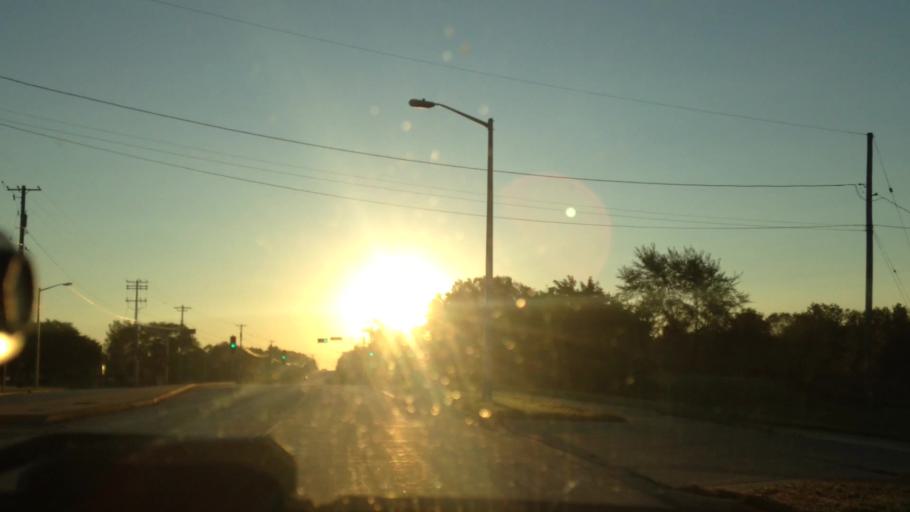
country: US
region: Wisconsin
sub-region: Washington County
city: West Bend
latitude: 43.4267
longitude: -88.1629
